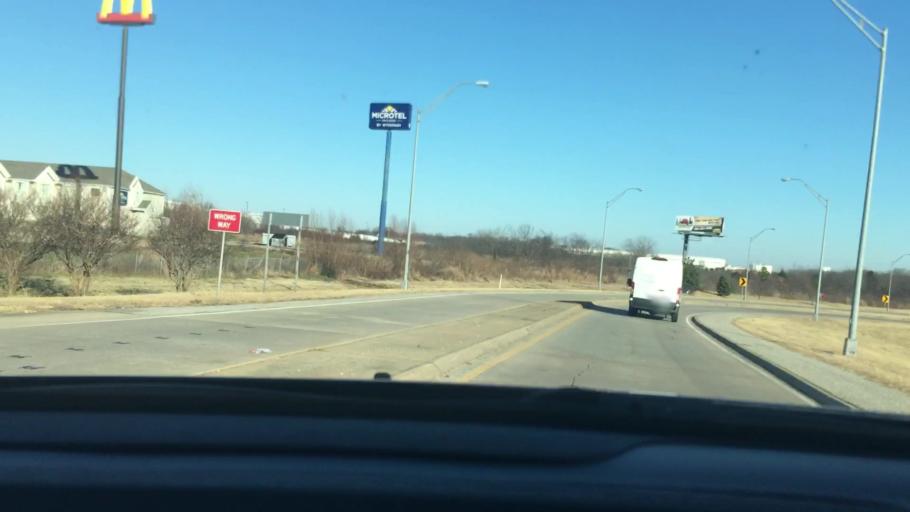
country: US
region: Oklahoma
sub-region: Carter County
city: Ardmore
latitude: 34.1878
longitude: -97.1687
